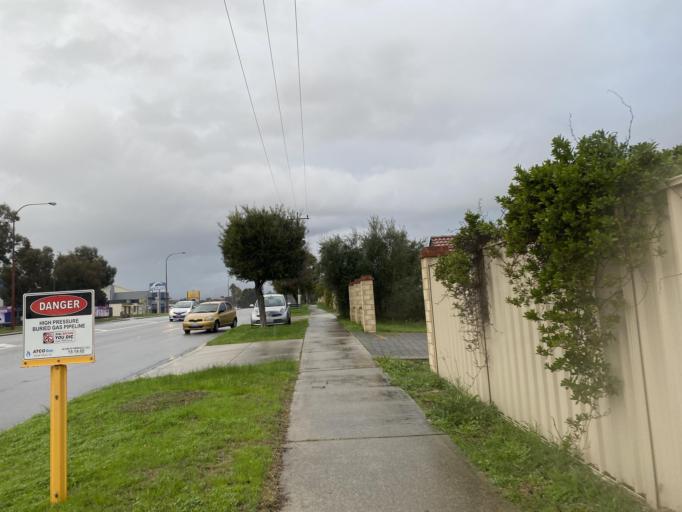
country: AU
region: Western Australia
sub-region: Canning
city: Queens Park
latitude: -31.9977
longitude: 115.9509
